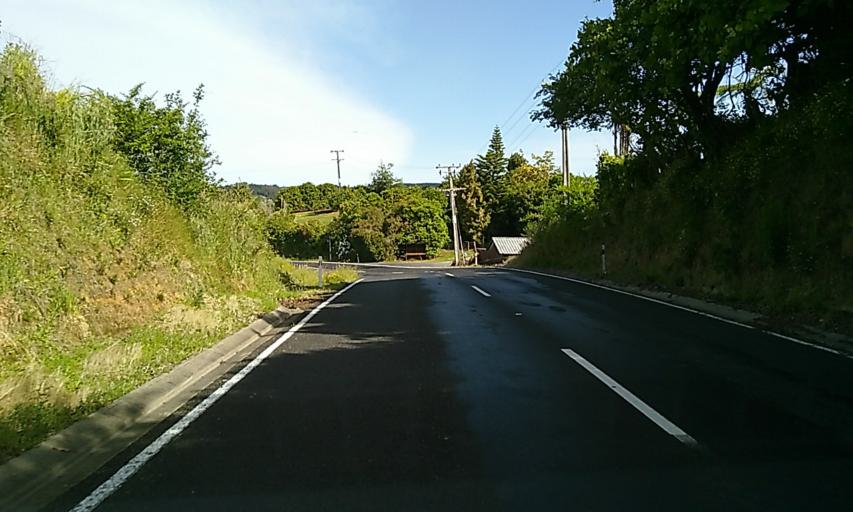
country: NZ
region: Bay of Plenty
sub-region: Tauranga City
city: Tauranga
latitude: -37.8012
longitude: 176.0410
